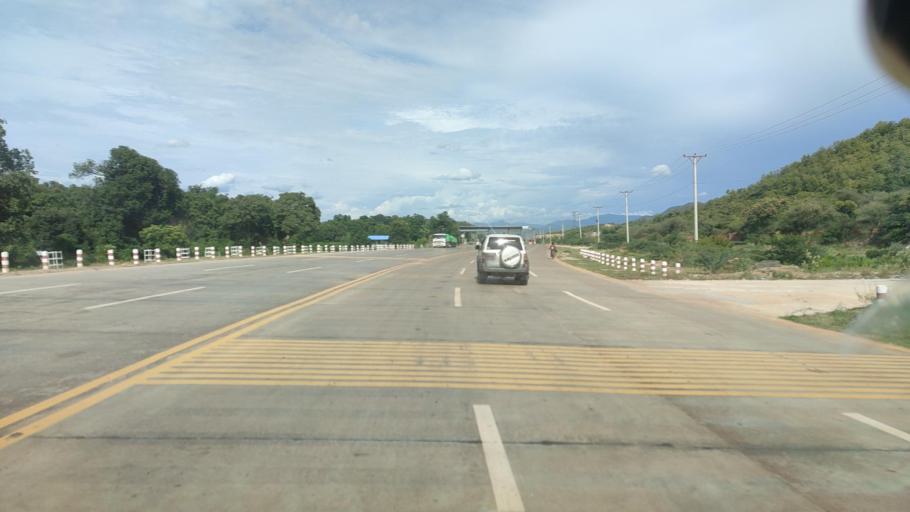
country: MM
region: Mandalay
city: Kyaukse
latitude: 21.6102
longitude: 96.1765
